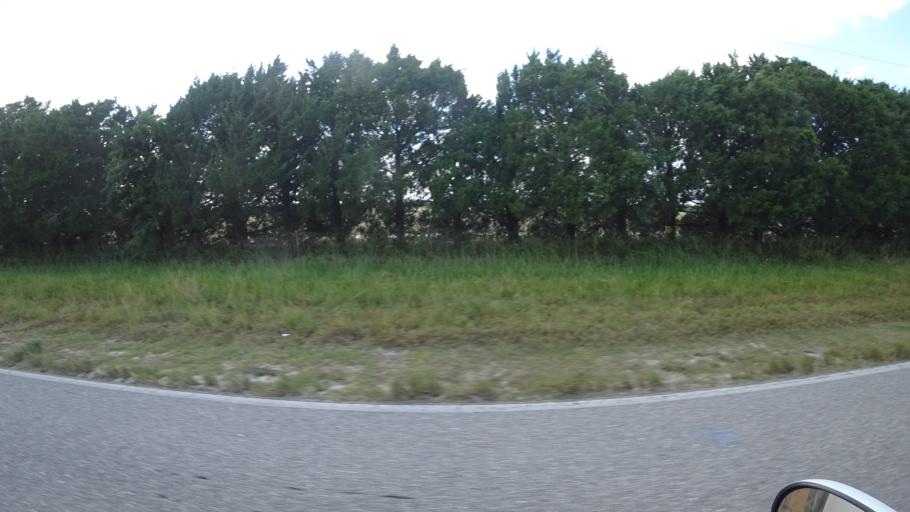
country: US
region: Florida
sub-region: DeSoto County
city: Arcadia
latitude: 27.2976
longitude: -82.1134
